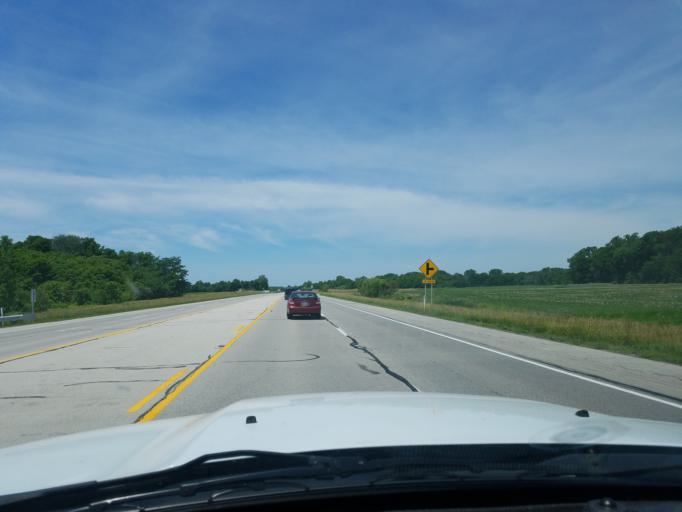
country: US
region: Indiana
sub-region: Delaware County
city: Yorktown
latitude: 40.1206
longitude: -85.4594
